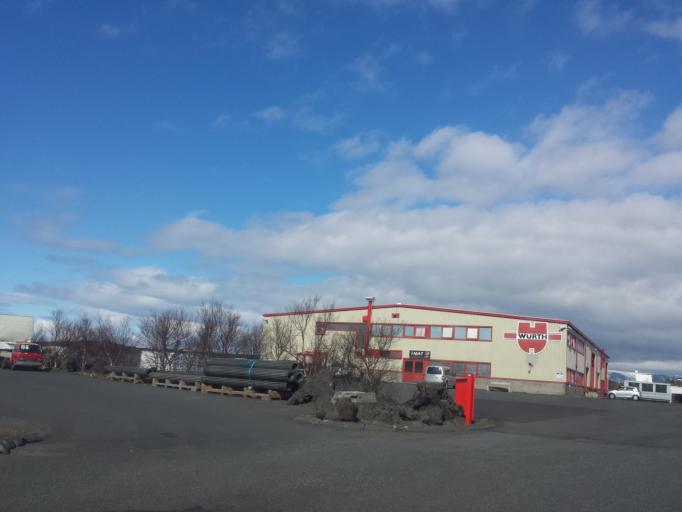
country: IS
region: Capital Region
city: Gardabaer
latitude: 64.0809
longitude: -21.9301
